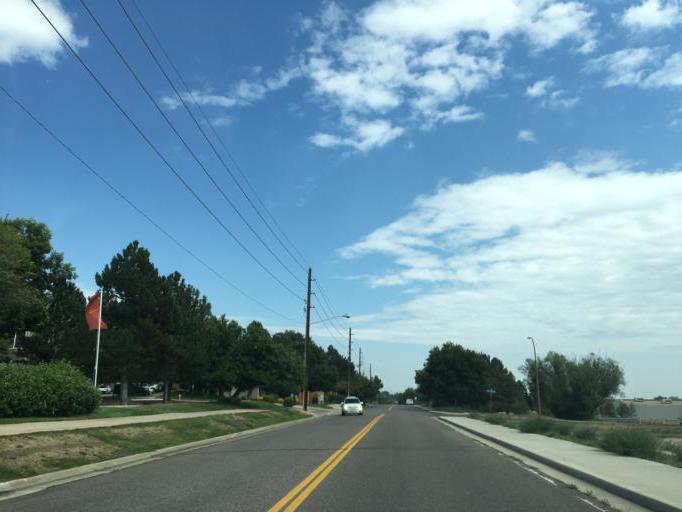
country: US
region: Colorado
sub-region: Jefferson County
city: Applewood
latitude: 39.7438
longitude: -105.1210
